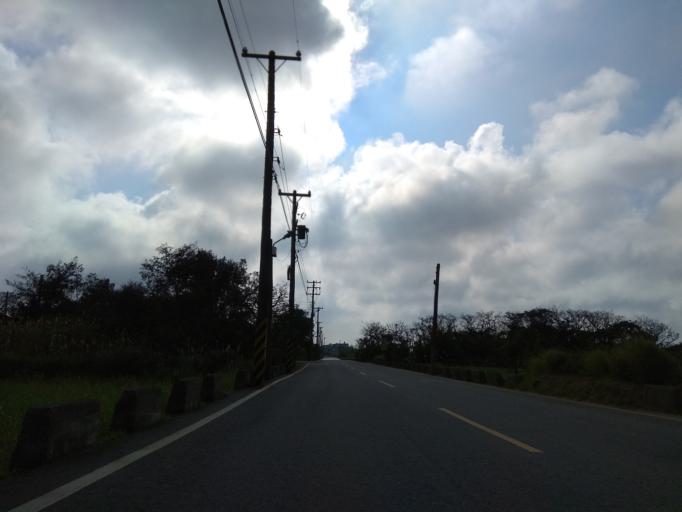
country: TW
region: Taiwan
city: Taoyuan City
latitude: 25.0613
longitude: 121.1537
